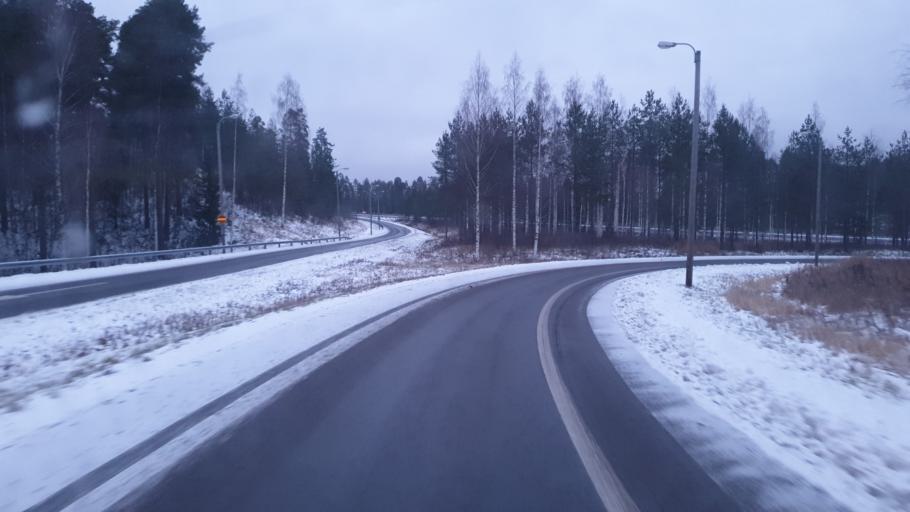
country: FI
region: Northern Savo
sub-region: Kuopio
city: Siilinjaervi
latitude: 63.0600
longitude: 27.6686
